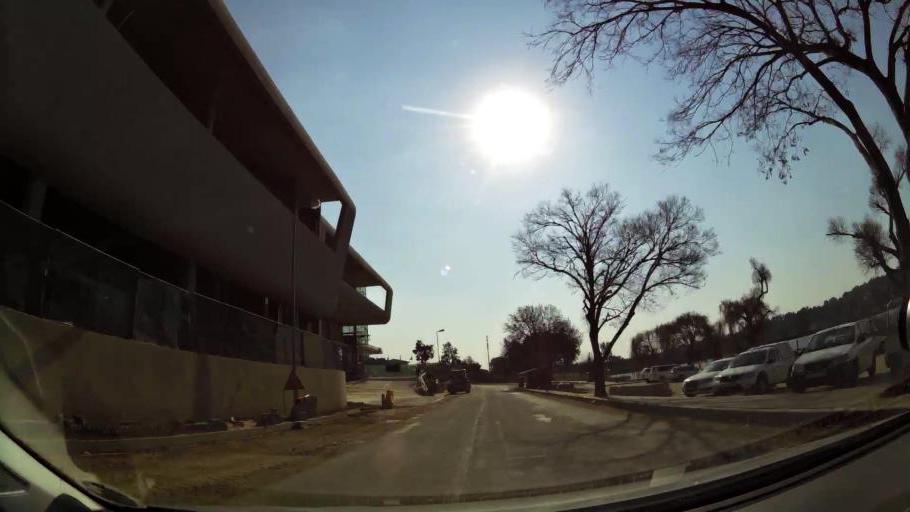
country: ZA
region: Gauteng
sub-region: City of Johannesburg Metropolitan Municipality
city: Modderfontein
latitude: -26.0986
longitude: 28.1518
